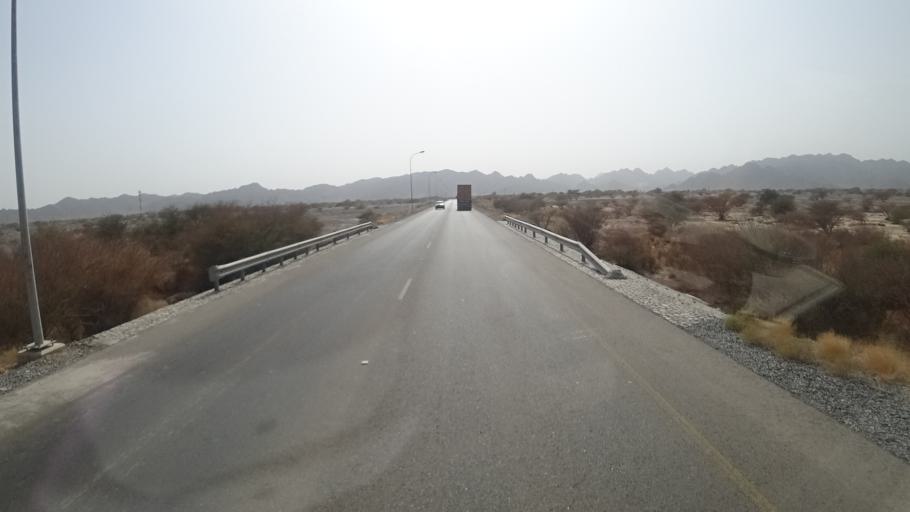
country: OM
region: Muhafazat ad Dakhiliyah
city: Nizwa
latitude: 22.9973
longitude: 57.5480
